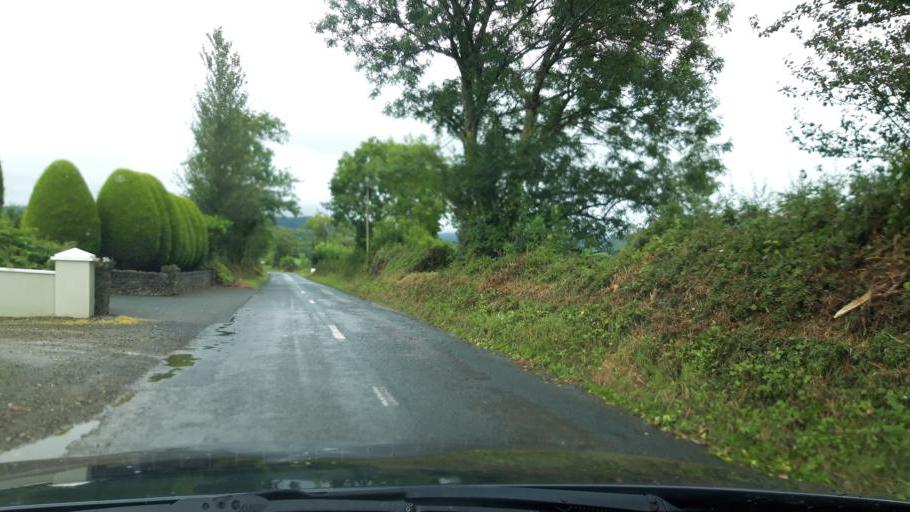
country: IE
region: Munster
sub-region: County Cork
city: Youghal
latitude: 52.1685
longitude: -7.8524
